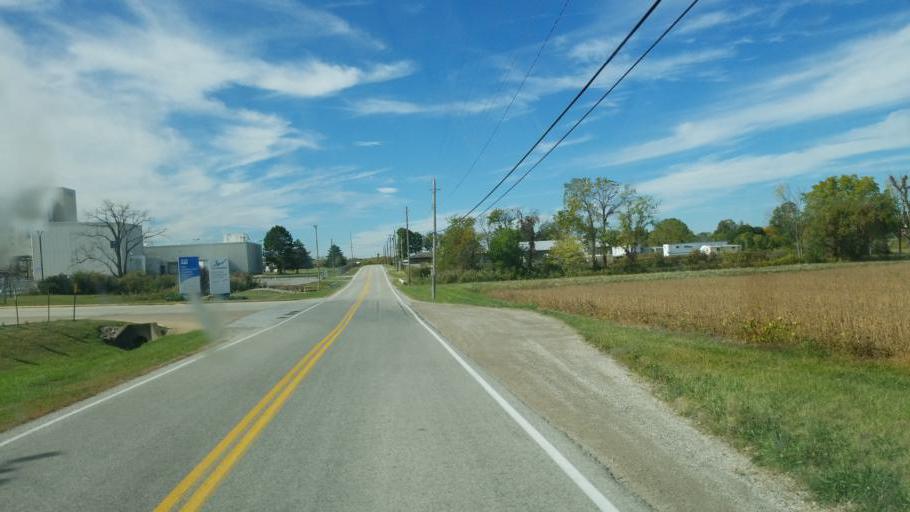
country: US
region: Ohio
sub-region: Erie County
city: Huron
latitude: 41.3731
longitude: -82.5391
